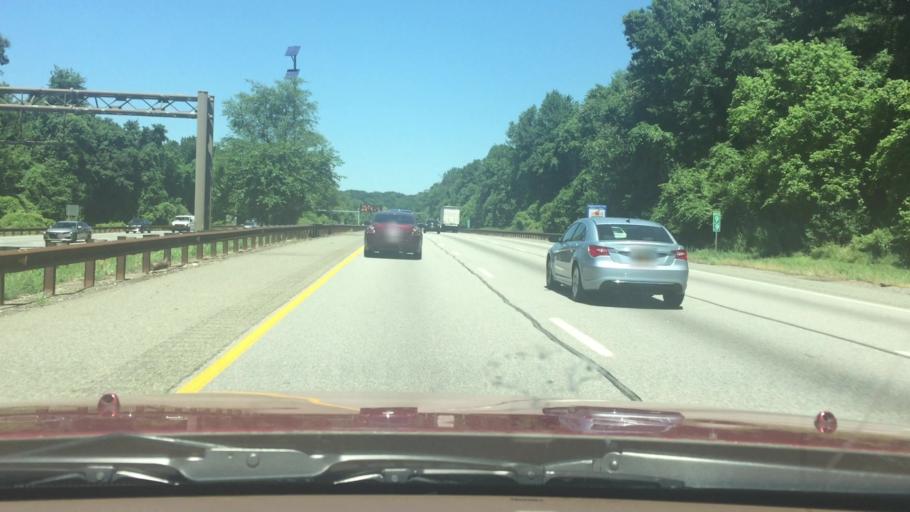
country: US
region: Pennsylvania
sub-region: Delaware County
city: Broomall
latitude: 39.9944
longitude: -75.3463
